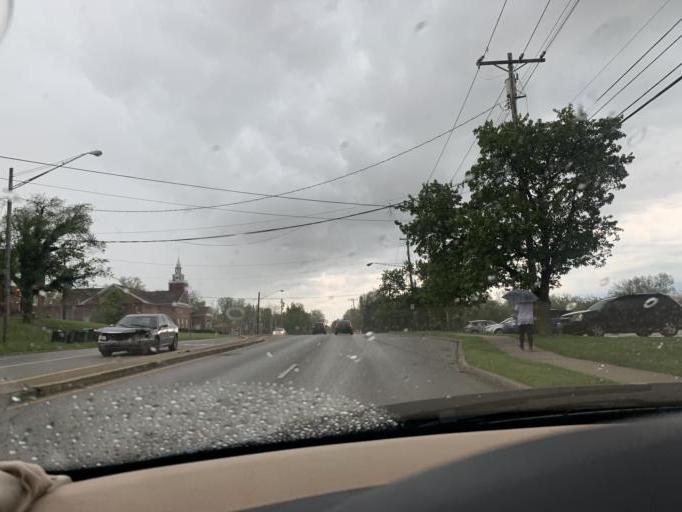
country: US
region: Ohio
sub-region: Hamilton County
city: Golf Manor
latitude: 39.1915
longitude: -84.4619
